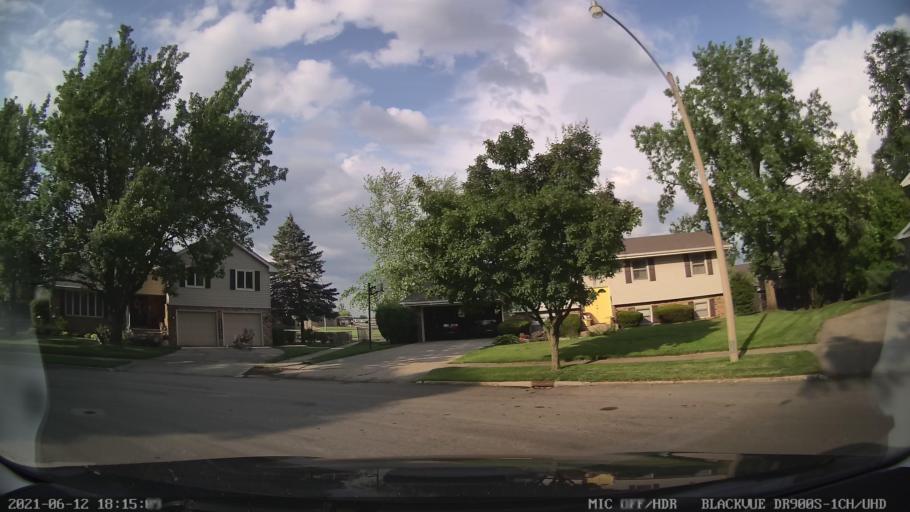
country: US
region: Illinois
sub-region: McLean County
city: Bloomington
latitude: 40.4782
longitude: -88.9596
